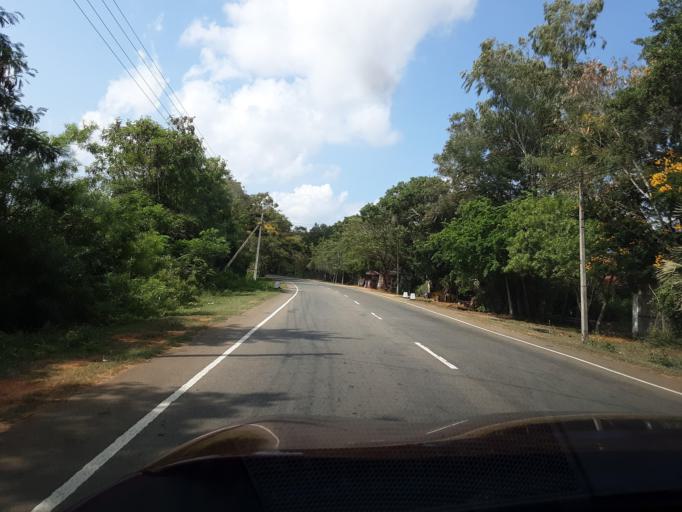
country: LK
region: Southern
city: Tangalla
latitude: 6.2456
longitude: 81.2277
